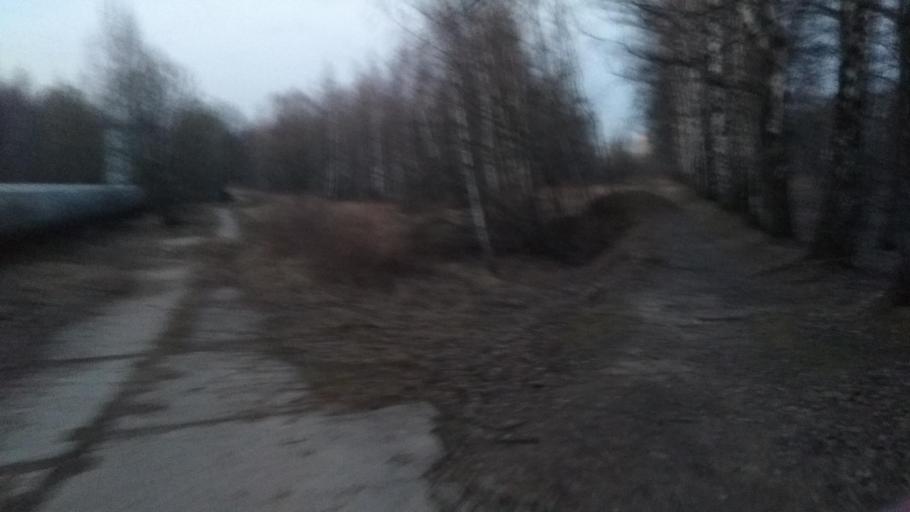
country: RU
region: Moscow
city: Biryulevo
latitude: 55.5900
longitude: 37.7021
